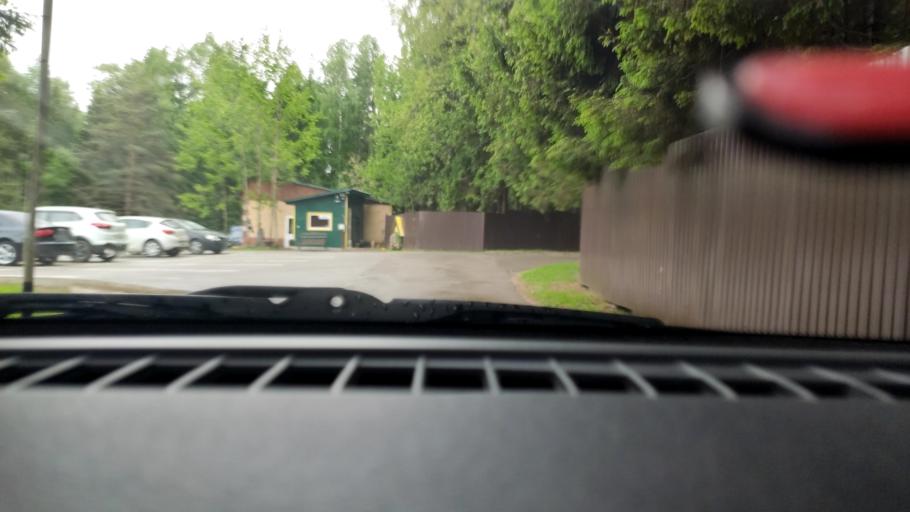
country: RU
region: Perm
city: Karagay
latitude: 58.2372
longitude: 54.8733
